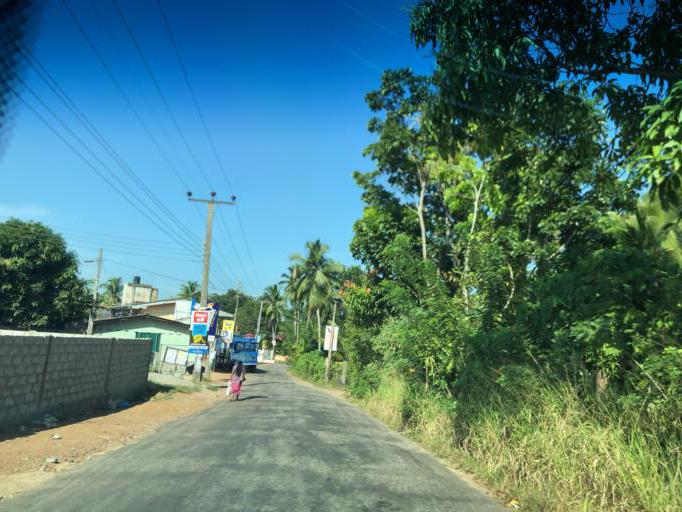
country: LK
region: Western
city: Homagama
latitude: 6.8088
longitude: 79.9781
